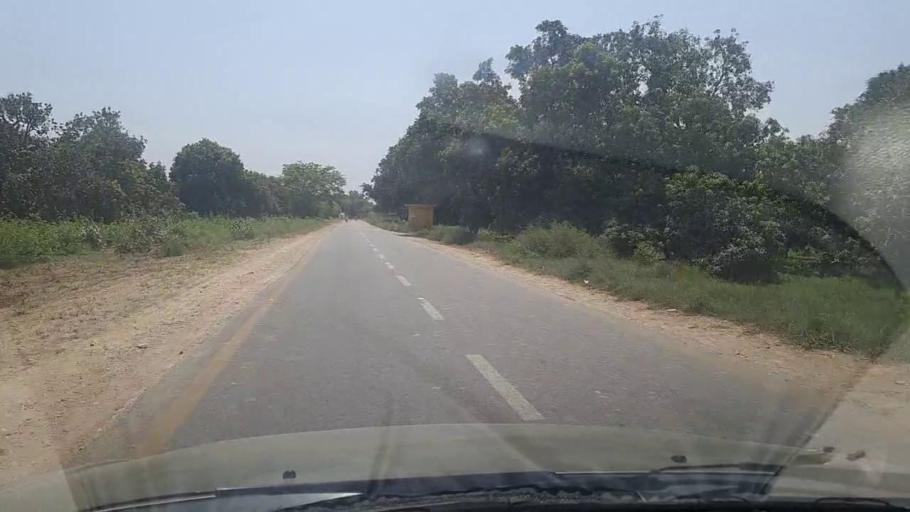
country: PK
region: Sindh
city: Tando Jam
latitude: 25.3440
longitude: 68.5187
